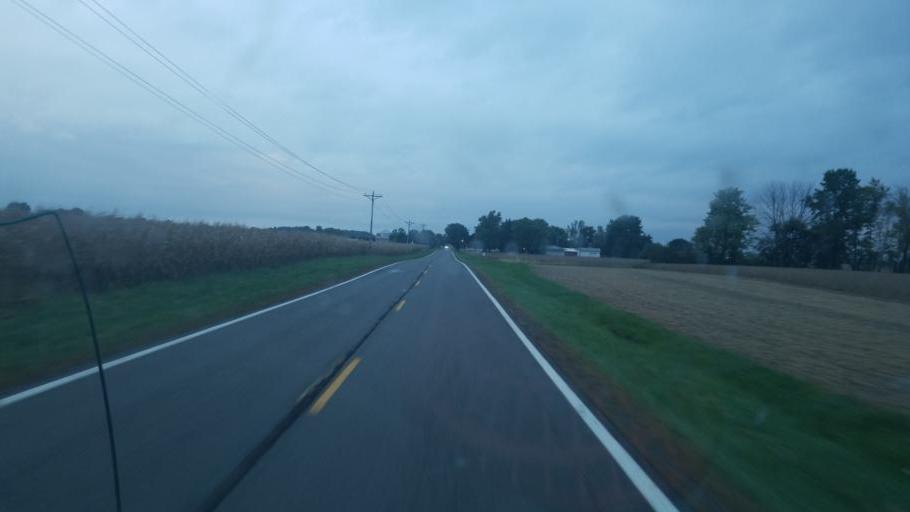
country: US
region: Ohio
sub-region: Morrow County
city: Cardington
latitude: 40.5970
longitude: -82.9623
